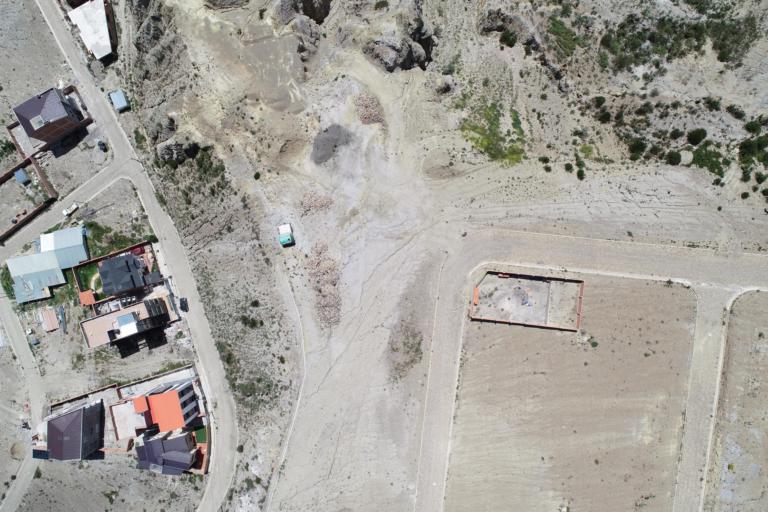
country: BO
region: La Paz
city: La Paz
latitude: -16.5220
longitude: -68.0492
